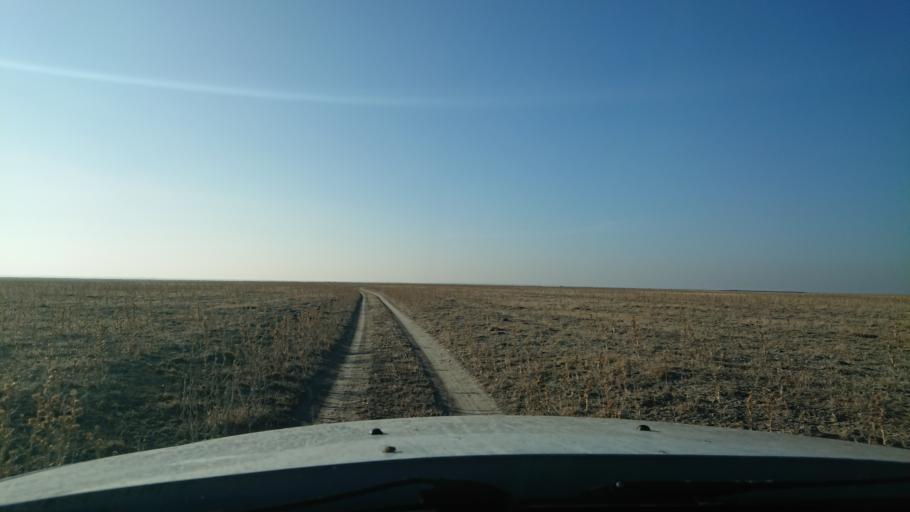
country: TR
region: Aksaray
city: Sultanhani
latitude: 38.3719
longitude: 33.5444
